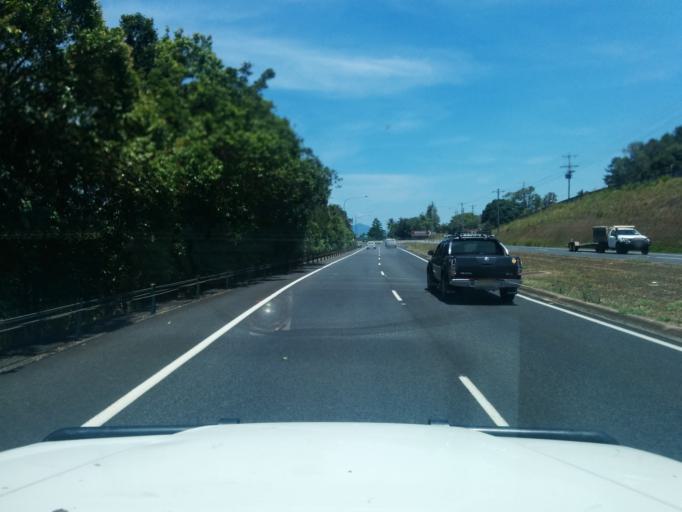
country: AU
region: Queensland
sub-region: Cairns
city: Redlynch
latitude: -16.9110
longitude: 145.7159
